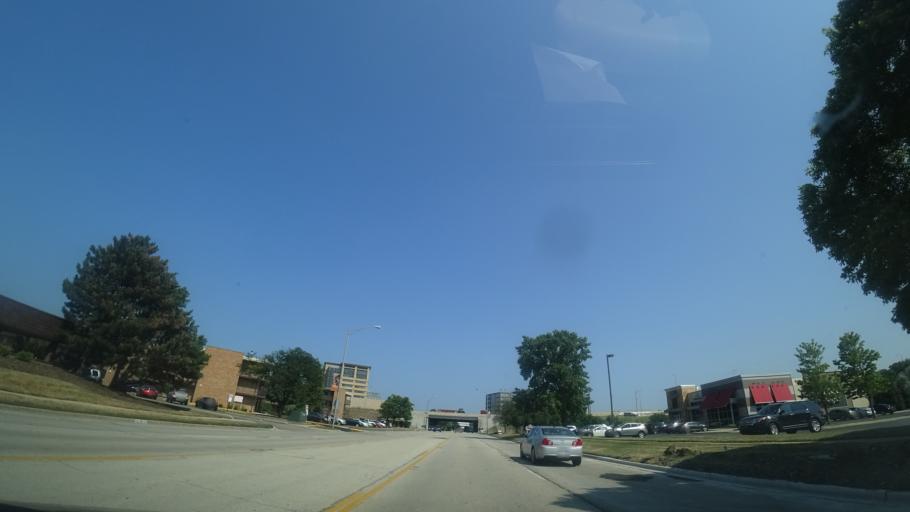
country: US
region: Illinois
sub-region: Cook County
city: Rosemont
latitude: 41.9940
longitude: -87.8689
